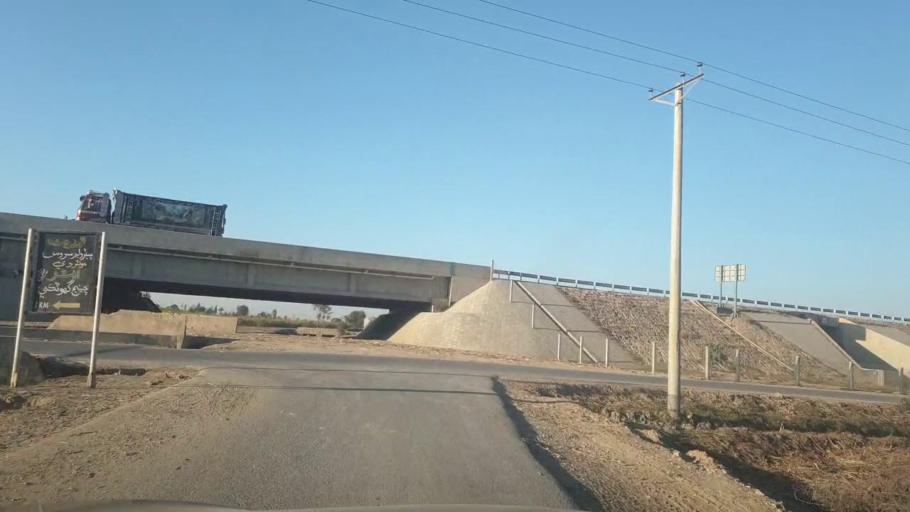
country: PK
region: Sindh
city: Ghotki
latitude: 28.0072
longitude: 69.2695
